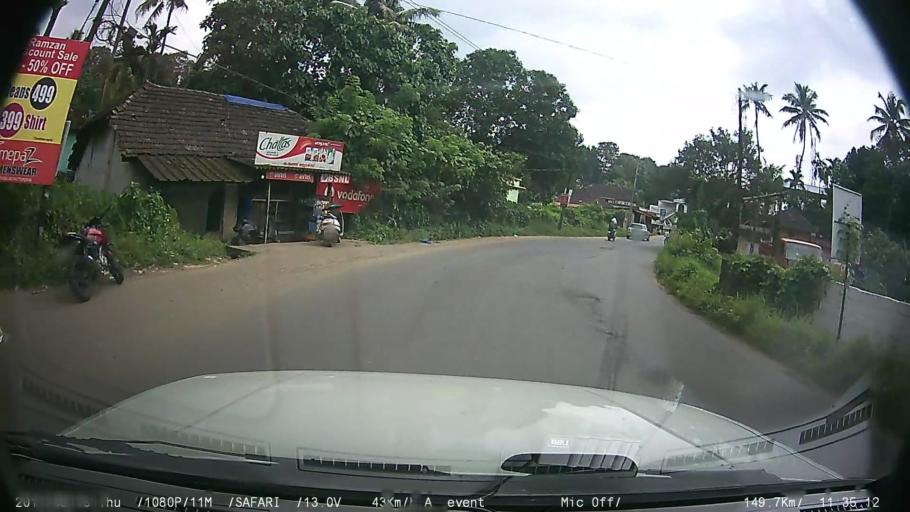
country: IN
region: Kerala
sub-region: Ernakulam
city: Muvattupula
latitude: 9.9967
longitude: 76.5942
